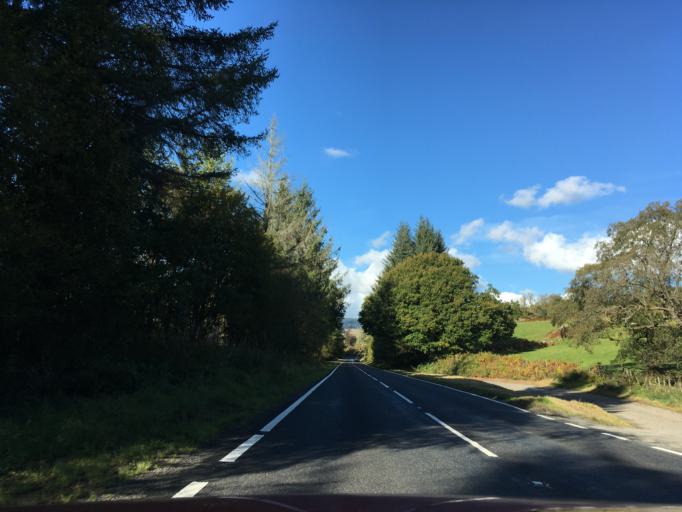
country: GB
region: Wales
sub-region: Merthyr Tydfil County Borough
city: Merthyr Tydfil
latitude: 51.7994
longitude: -3.4384
